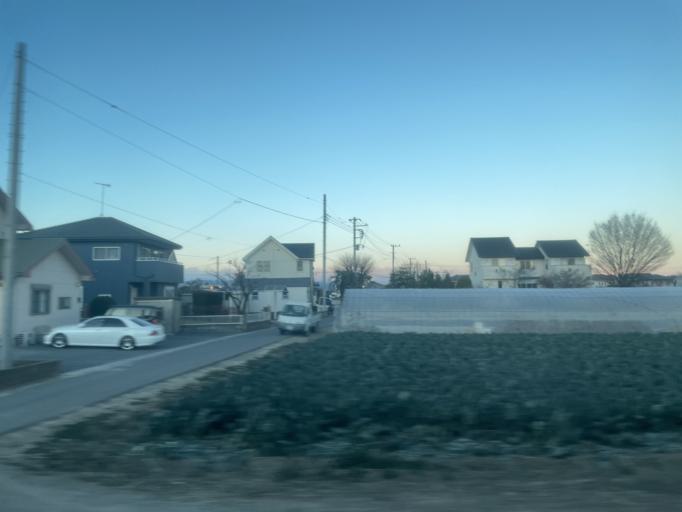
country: JP
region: Saitama
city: Fukayacho
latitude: 36.2021
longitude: 139.2460
